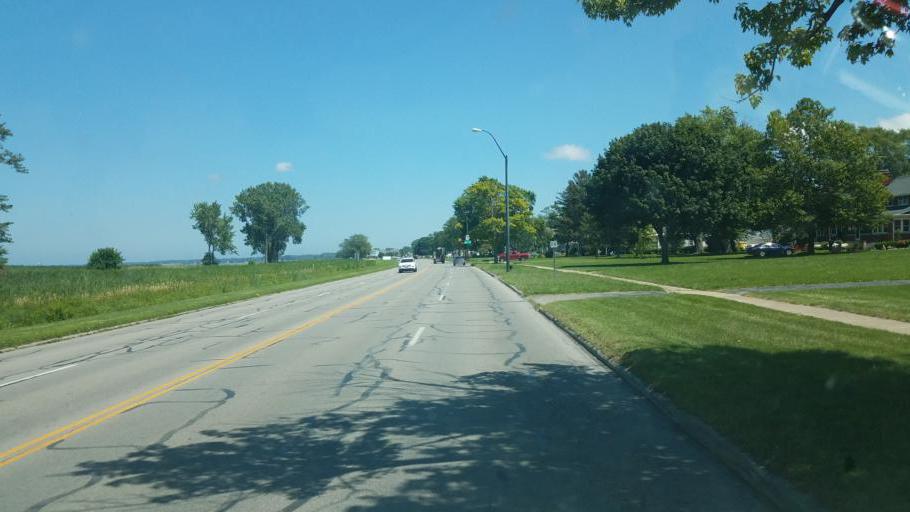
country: US
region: Ohio
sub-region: Ottawa County
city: Port Clinton
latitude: 41.5136
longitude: -82.9318
